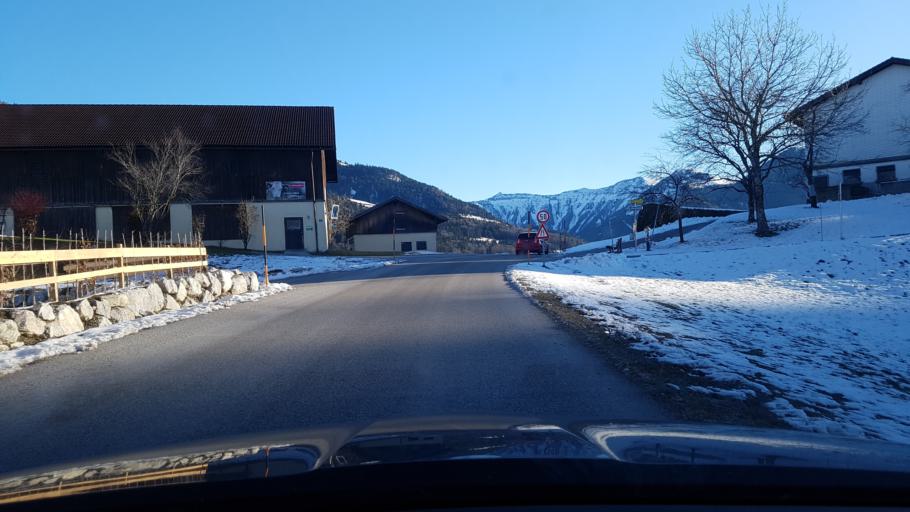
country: AT
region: Salzburg
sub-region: Politischer Bezirk Hallein
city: Kuchl
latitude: 47.6568
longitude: 13.1918
